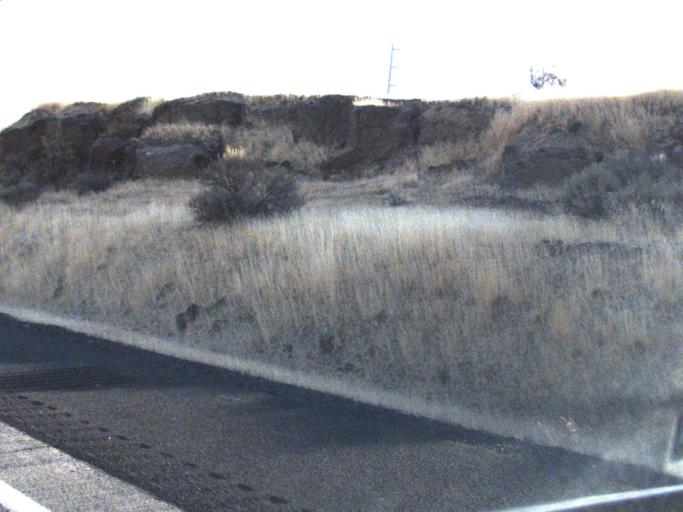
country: US
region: Washington
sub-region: Franklin County
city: Connell
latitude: 46.6440
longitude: -118.8575
